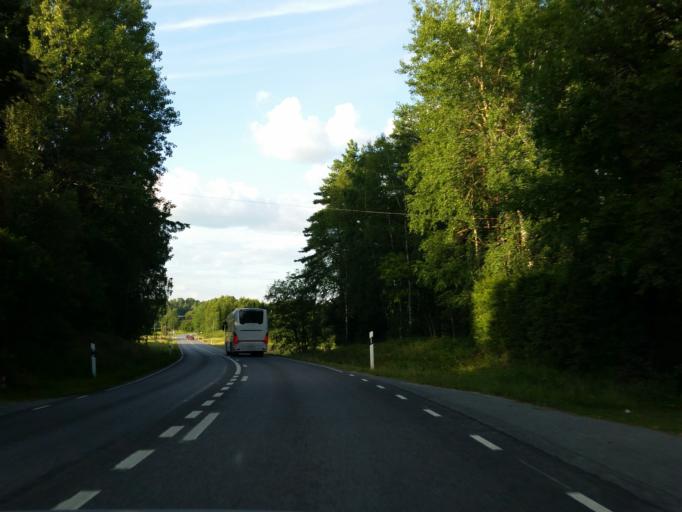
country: SE
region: Stockholm
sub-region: Sodertalje Kommun
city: Molnbo
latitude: 59.0709
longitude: 17.5356
